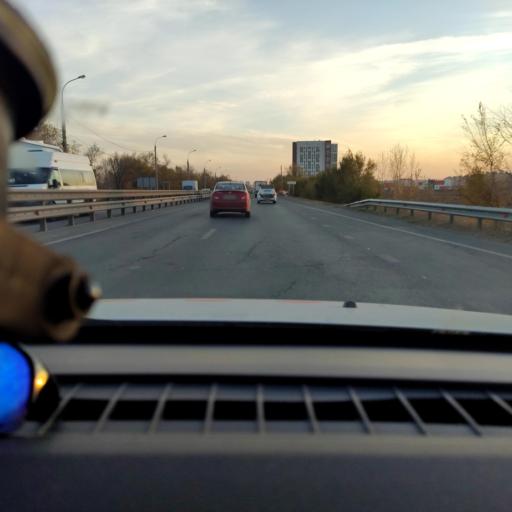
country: RU
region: Samara
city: Samara
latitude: 53.1229
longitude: 50.1693
